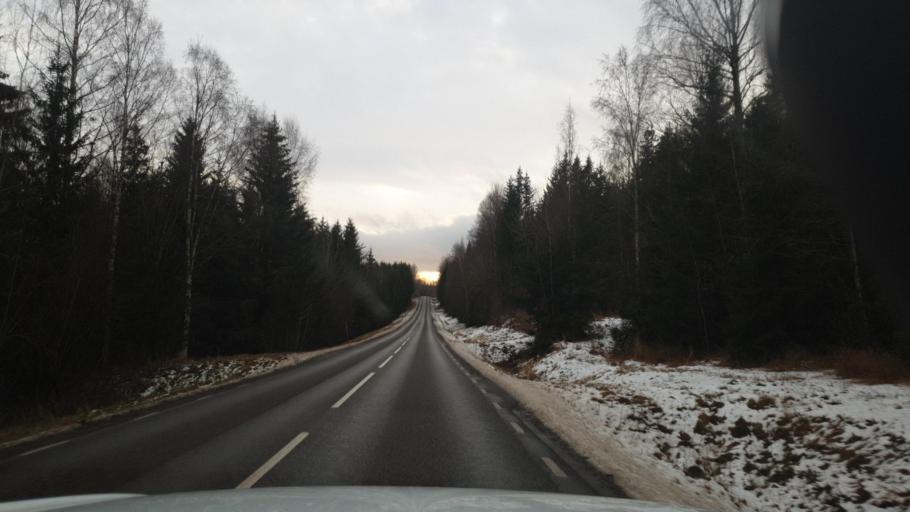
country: SE
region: Vaermland
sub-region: Eda Kommun
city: Amotfors
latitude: 59.7268
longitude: 12.4224
